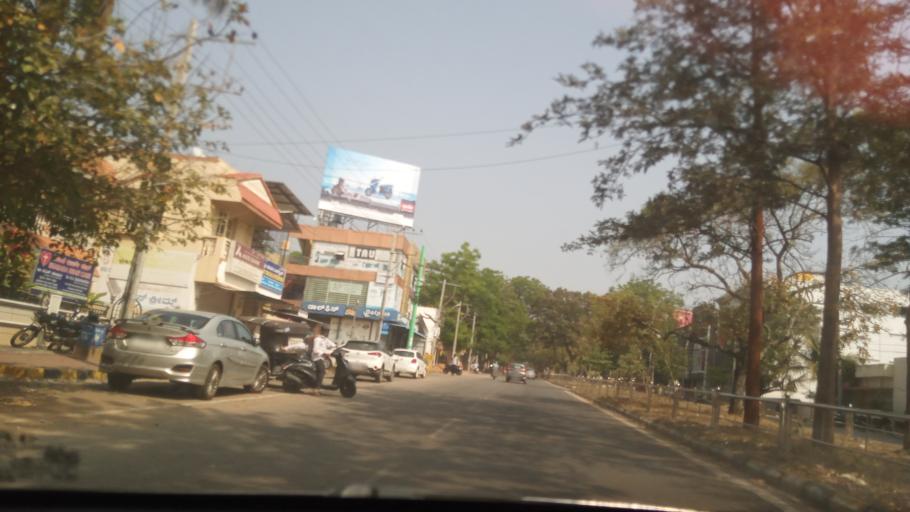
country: IN
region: Karnataka
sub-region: Mysore
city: Mysore
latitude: 12.3003
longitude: 76.6262
